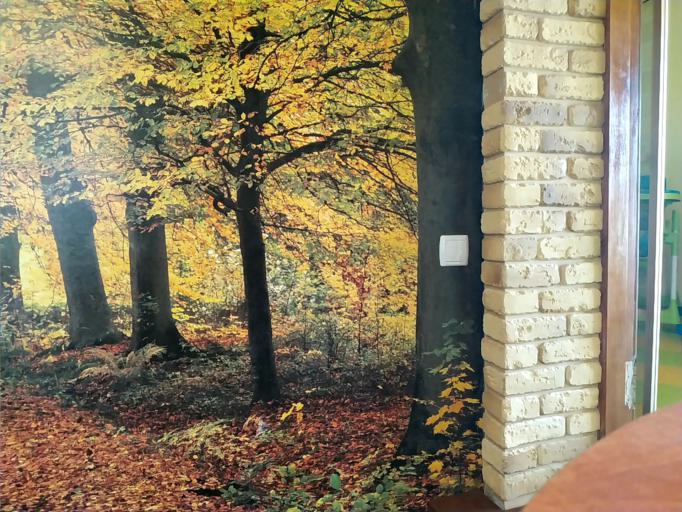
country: RU
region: Tverskaya
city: Rameshki
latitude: 57.5580
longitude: 35.9491
